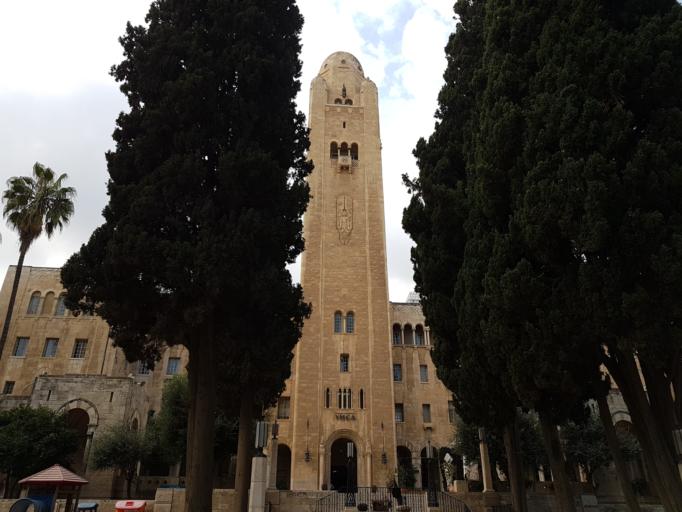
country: IL
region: Jerusalem
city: Jerusalem
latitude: 31.7743
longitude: 35.2219
